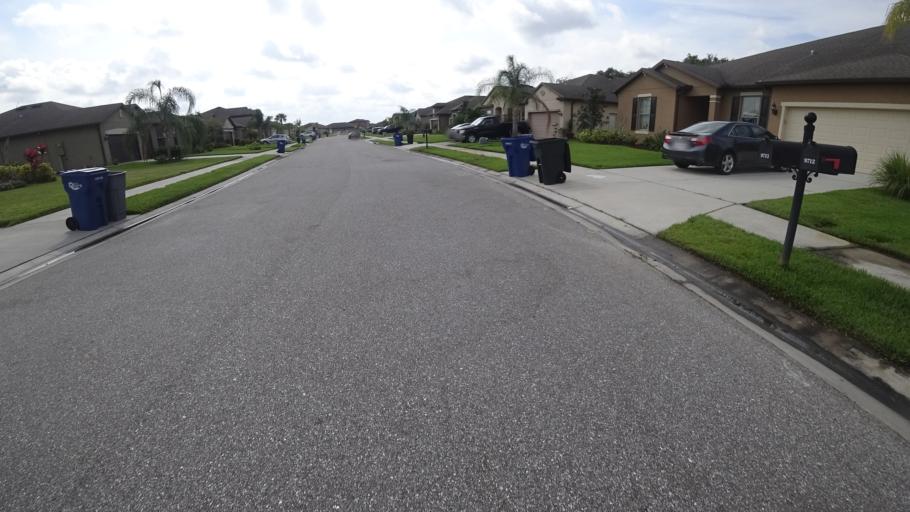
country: US
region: Florida
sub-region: Manatee County
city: Ellenton
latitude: 27.5691
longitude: -82.4682
